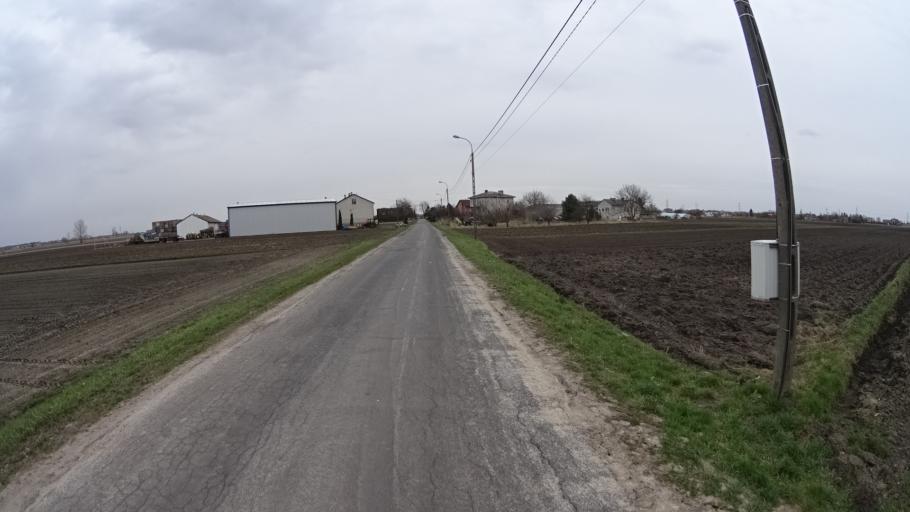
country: PL
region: Masovian Voivodeship
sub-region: Powiat warszawski zachodni
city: Ozarow Mazowiecki
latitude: 52.2456
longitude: 20.7503
